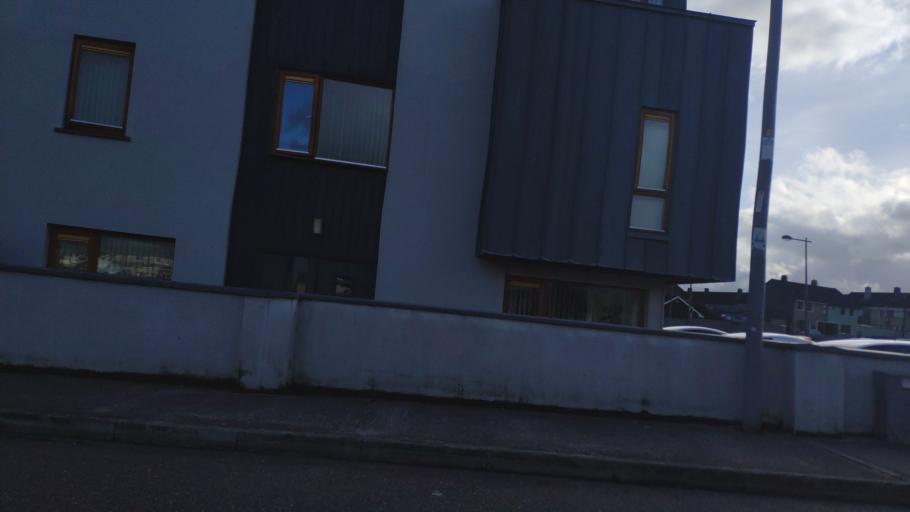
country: IE
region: Munster
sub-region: County Cork
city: Cork
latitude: 51.9099
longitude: -8.4897
